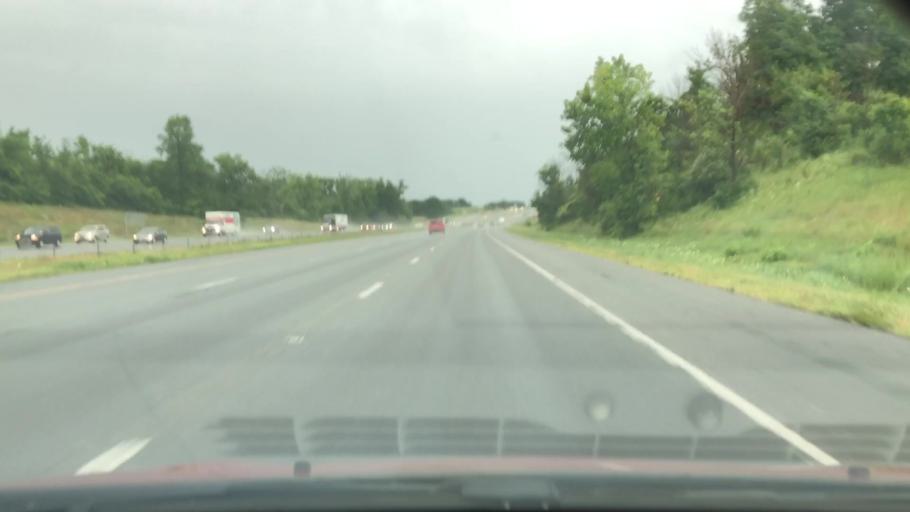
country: US
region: Ohio
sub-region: Madison County
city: Choctaw Lake
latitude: 39.9420
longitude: -83.5126
